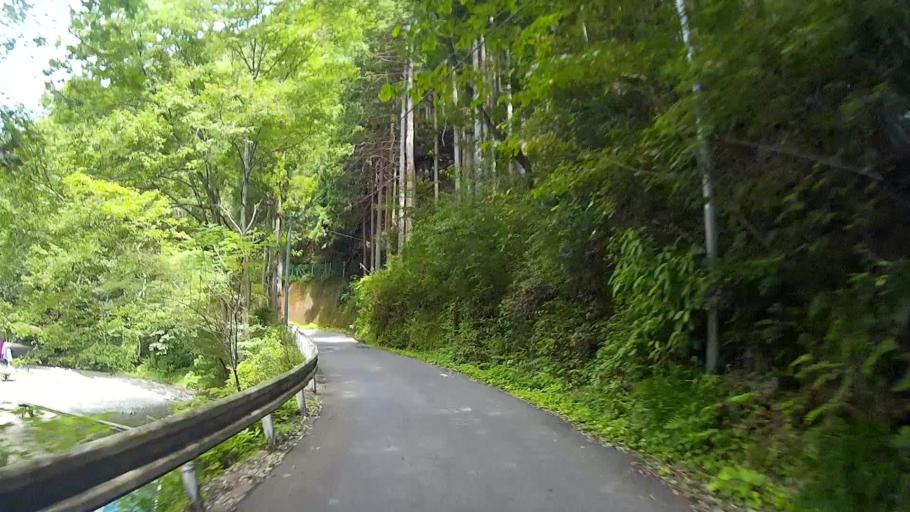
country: JP
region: Saitama
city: Chichibu
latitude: 35.9131
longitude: 139.1431
